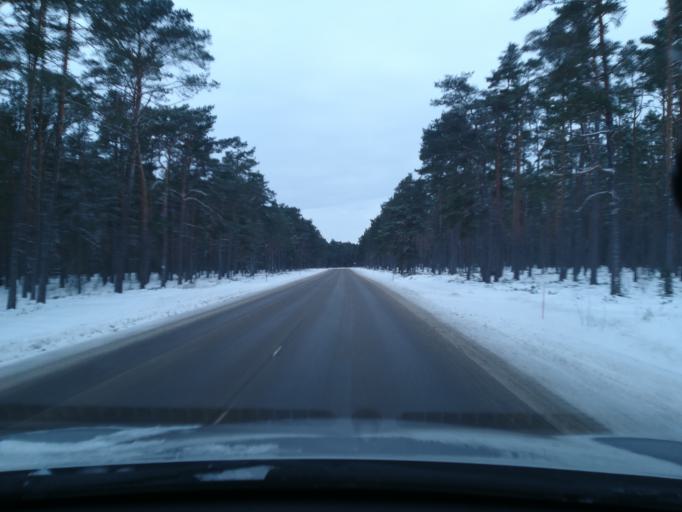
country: EE
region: Harju
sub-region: Keila linn
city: Keila
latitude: 59.4264
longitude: 24.3615
